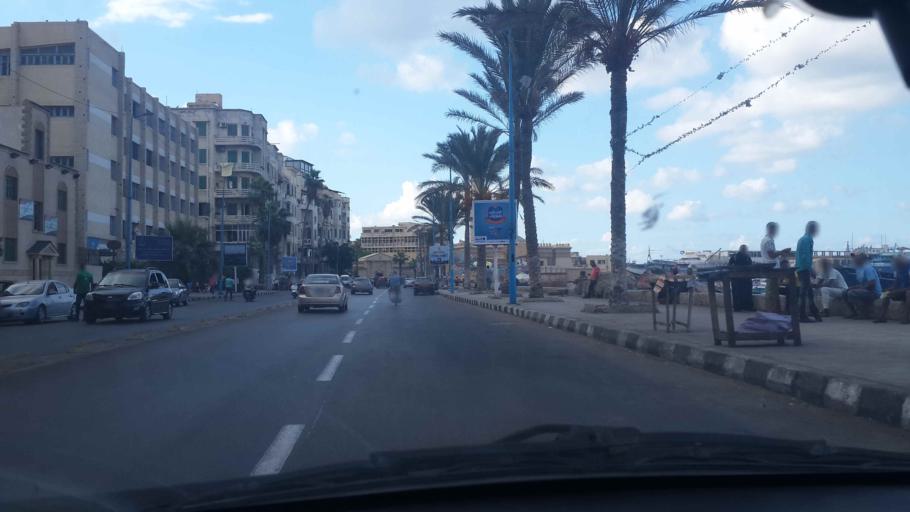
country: EG
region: Alexandria
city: Alexandria
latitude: 31.2083
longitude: 29.8830
